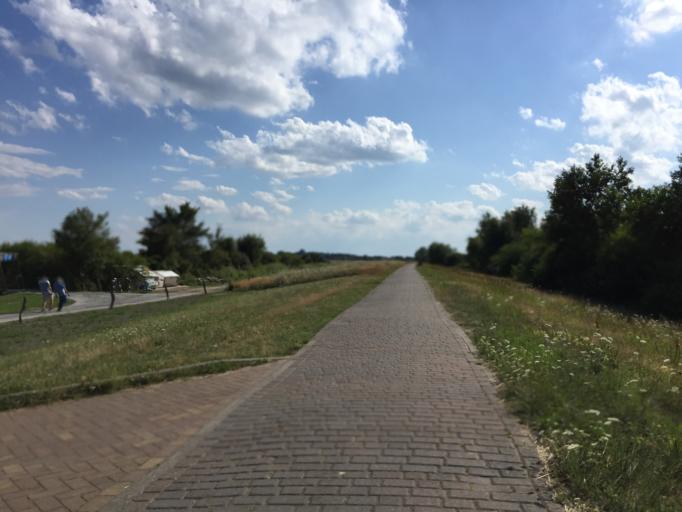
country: DE
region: Mecklenburg-Vorpommern
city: Hiddensee
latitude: 54.5840
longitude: 13.1101
